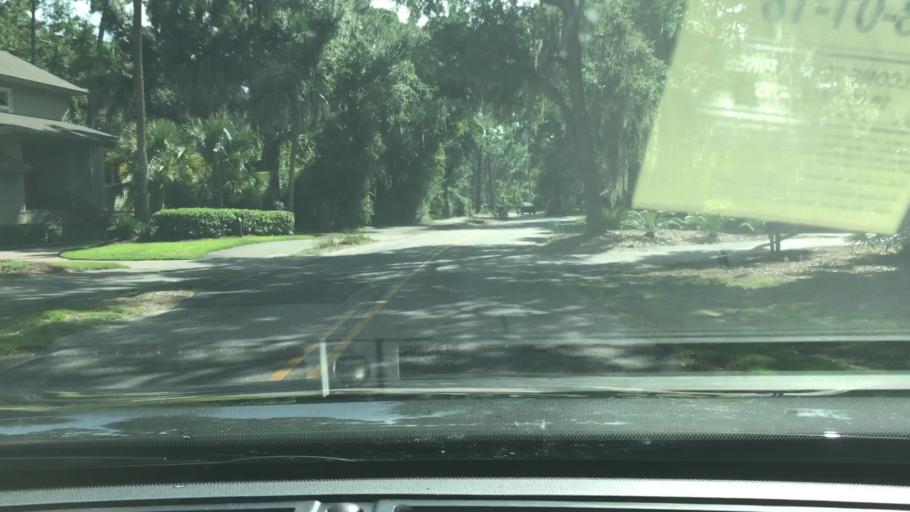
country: US
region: South Carolina
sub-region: Beaufort County
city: Hilton Head Island
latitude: 32.1284
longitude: -80.7840
